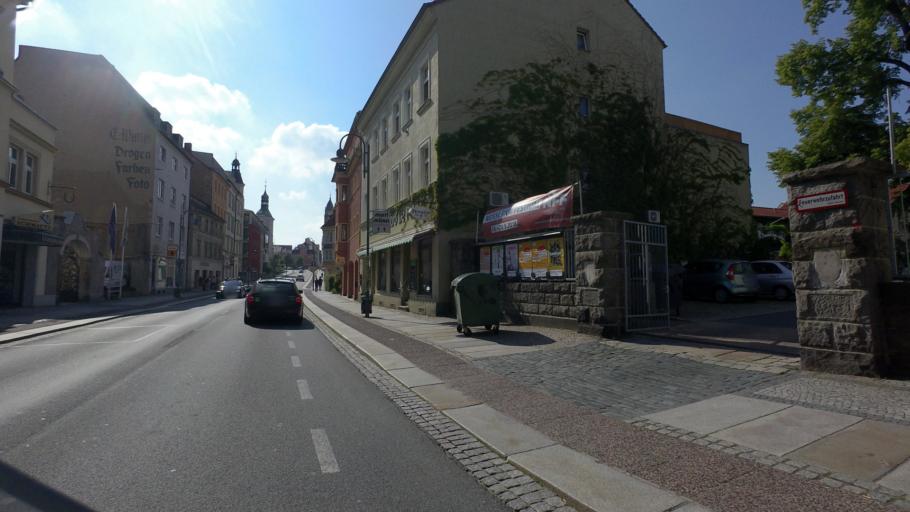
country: DE
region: Saxony
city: Bautzen
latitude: 51.1810
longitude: 14.4317
